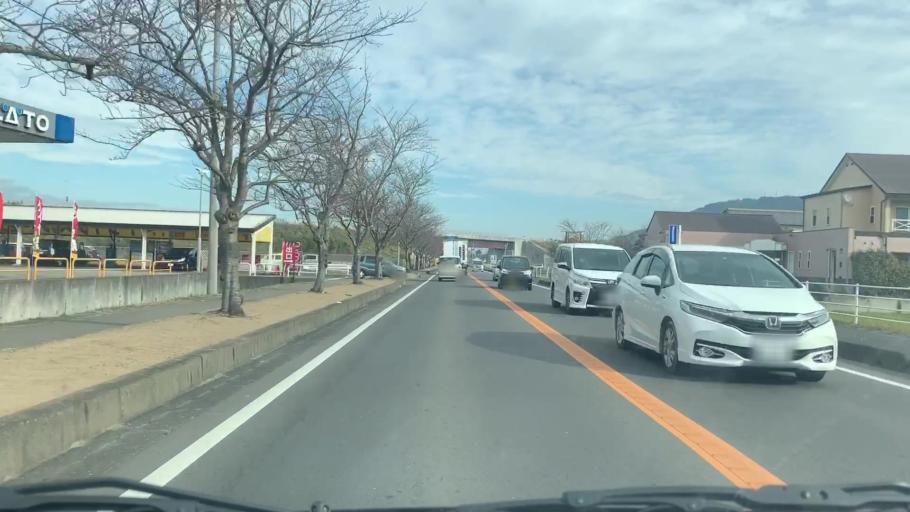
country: JP
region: Saga Prefecture
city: Karatsu
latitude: 33.4119
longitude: 129.9925
